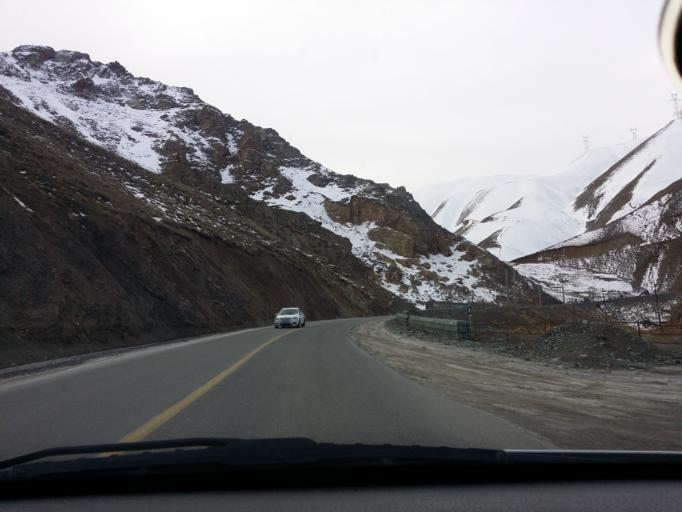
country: IR
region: Tehran
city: Tajrish
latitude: 36.1791
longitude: 51.3184
